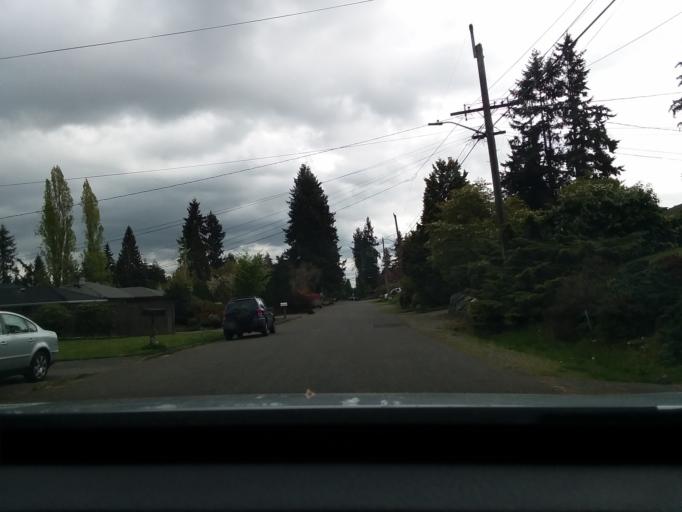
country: US
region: Washington
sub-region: King County
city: Shoreline
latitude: 47.7648
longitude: -122.3379
